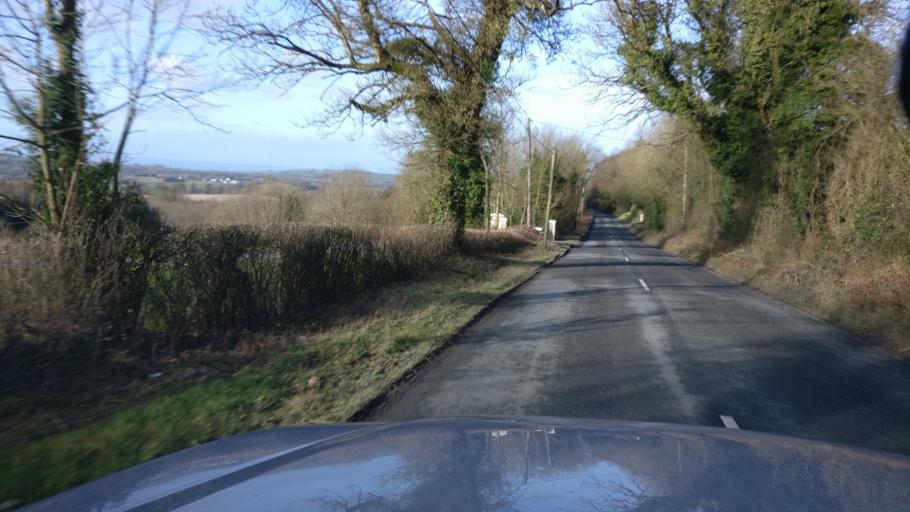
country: IE
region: Leinster
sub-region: Laois
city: Stradbally
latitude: 52.9401
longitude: -7.1987
